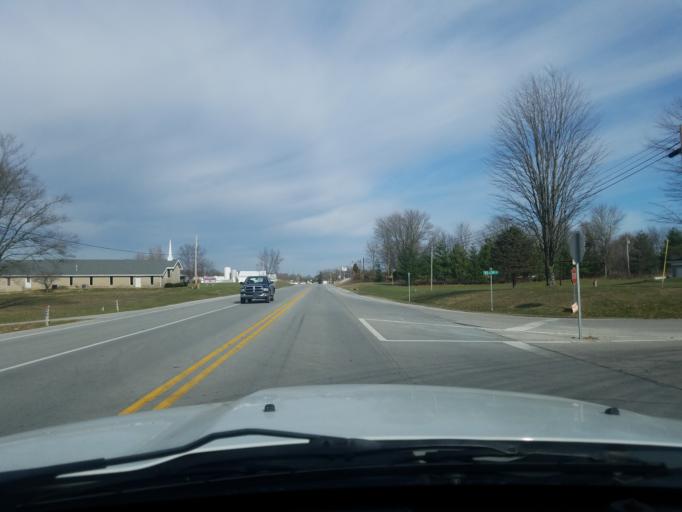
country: US
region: Indiana
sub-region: Orange County
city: Orleans
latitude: 38.6484
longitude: -86.4566
